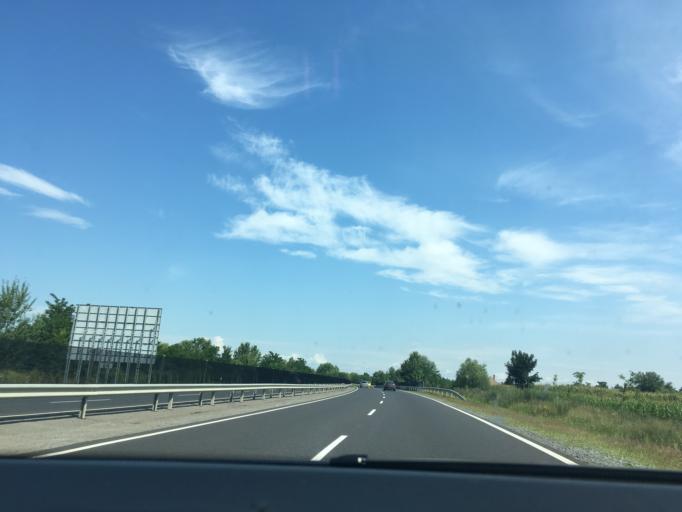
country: HU
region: Szabolcs-Szatmar-Bereg
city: Nyiregyhaza
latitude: 47.8887
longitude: 21.7108
